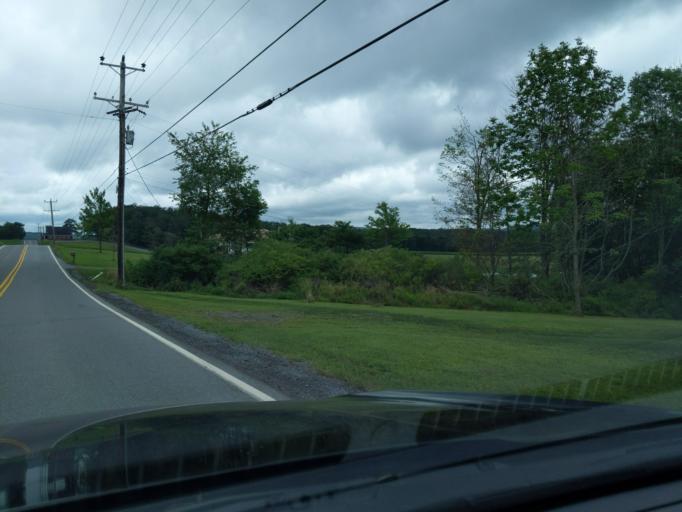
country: US
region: Pennsylvania
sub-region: Blair County
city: Claysburg
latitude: 40.3208
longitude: -78.5697
